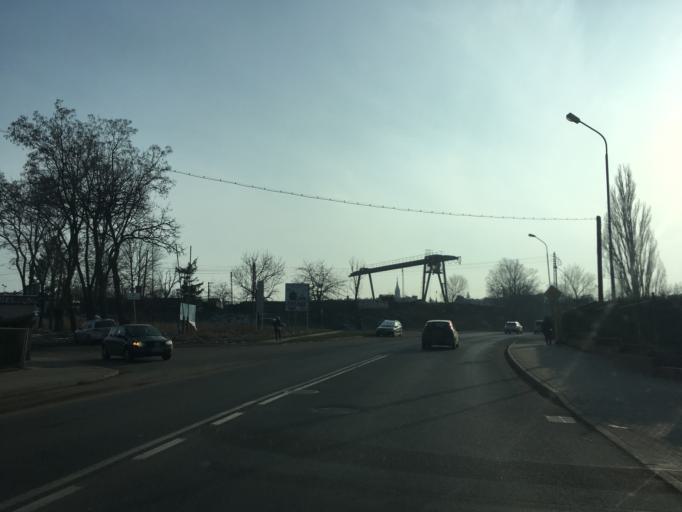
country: PL
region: Lower Silesian Voivodeship
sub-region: Powiat boleslawiecki
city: Boleslawiec
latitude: 51.2681
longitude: 15.5674
